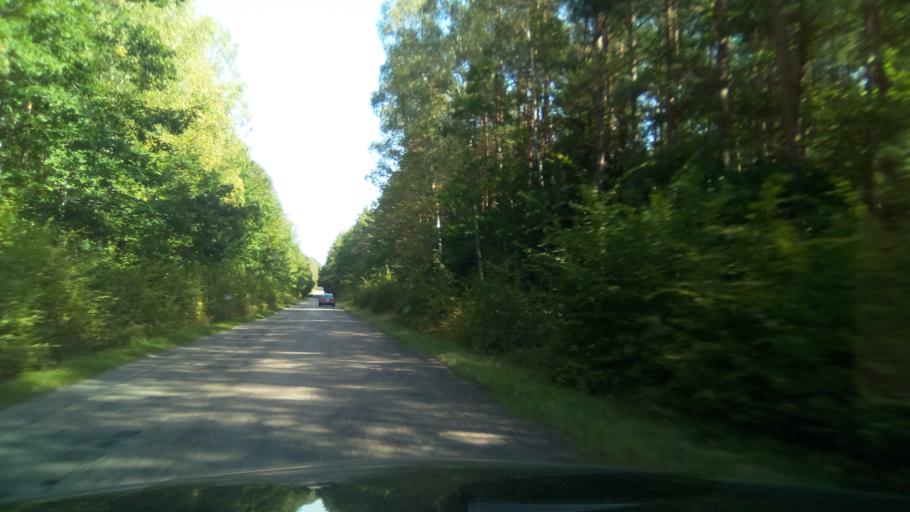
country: PL
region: Greater Poland Voivodeship
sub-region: Powiat zlotowski
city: Sypniewo
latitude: 53.4221
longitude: 16.5945
